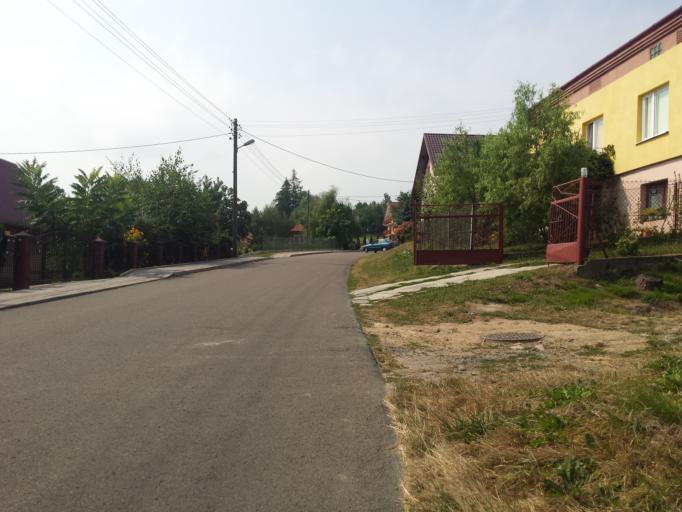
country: PL
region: Subcarpathian Voivodeship
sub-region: Powiat rzeszowski
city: Dynow
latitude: 49.8189
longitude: 22.2141
